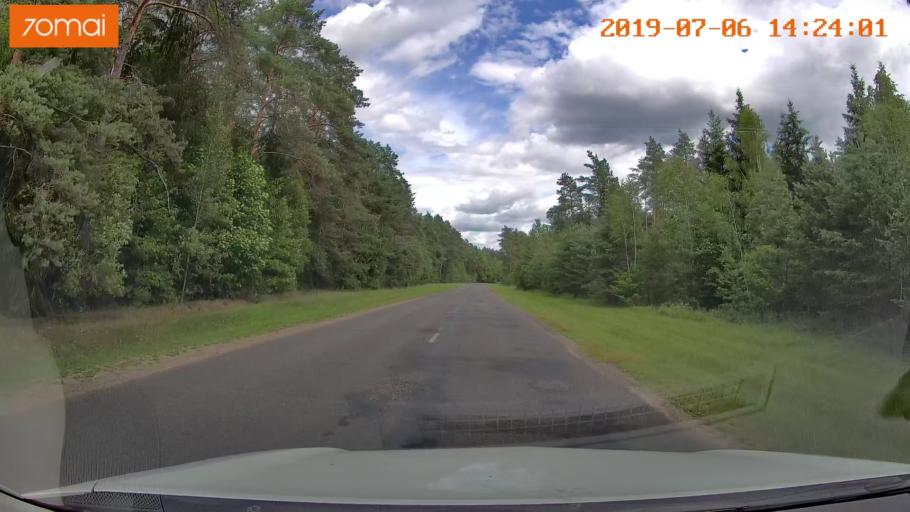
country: BY
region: Minsk
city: Ivyanyets
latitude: 53.9208
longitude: 26.7744
